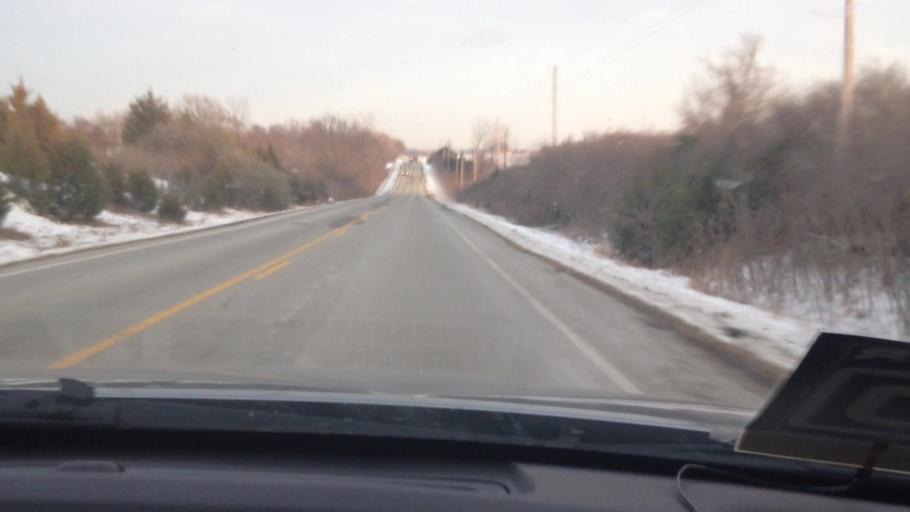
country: US
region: Kansas
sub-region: Leavenworth County
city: Lansing
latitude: 39.2377
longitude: -94.9277
